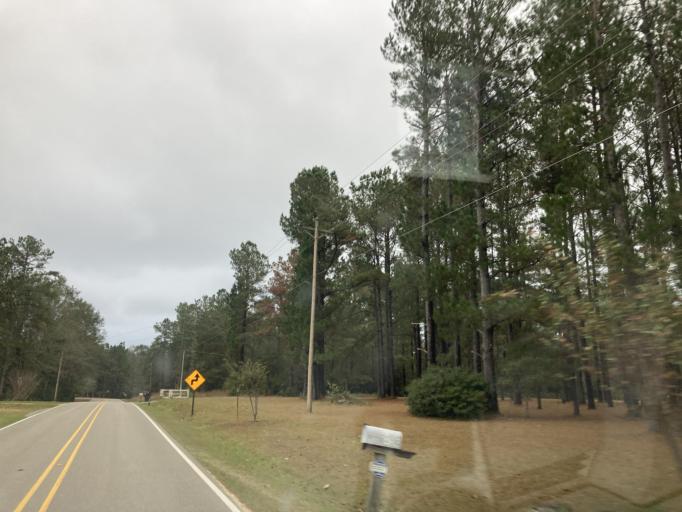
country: US
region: Mississippi
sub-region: Lamar County
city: Purvis
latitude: 31.1652
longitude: -89.4315
